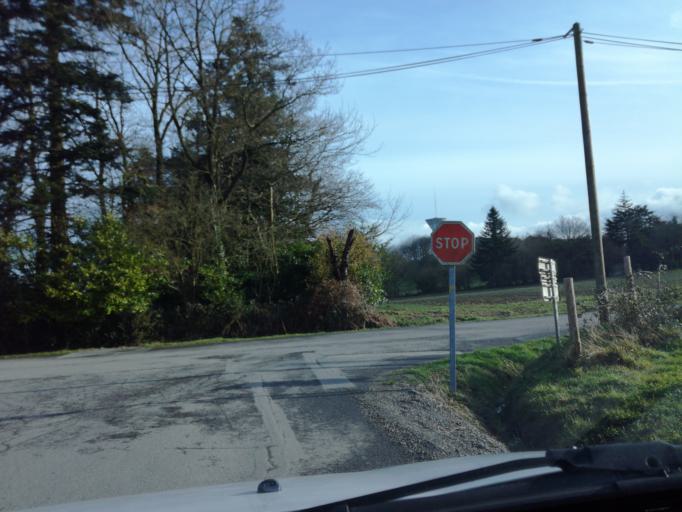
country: FR
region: Brittany
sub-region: Departement d'Ille-et-Vilaine
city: Liffre
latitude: 48.2013
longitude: -1.4927
